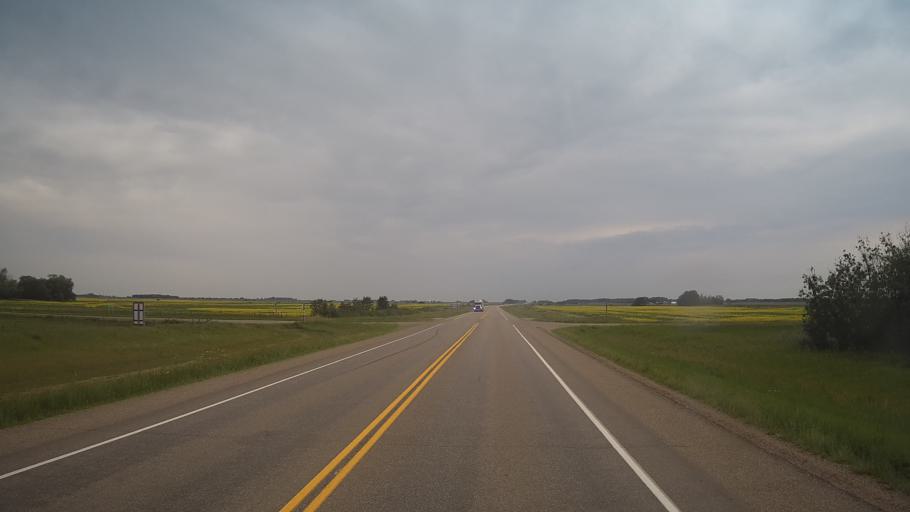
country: CA
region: Saskatchewan
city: Langham
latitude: 52.1284
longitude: -107.2398
